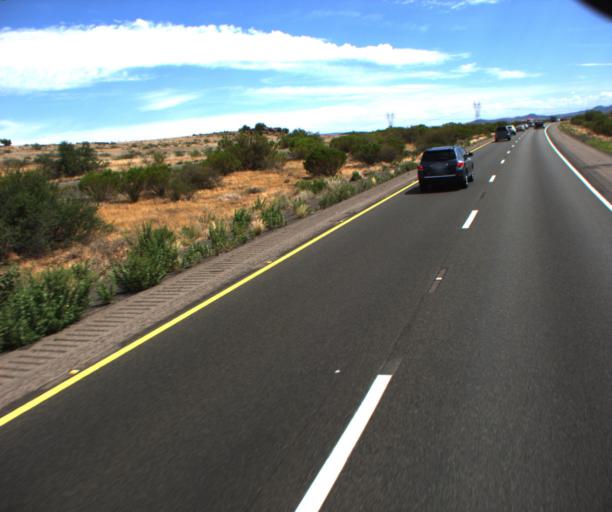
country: US
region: Arizona
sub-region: Yavapai County
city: Spring Valley
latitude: 34.3753
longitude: -112.1060
